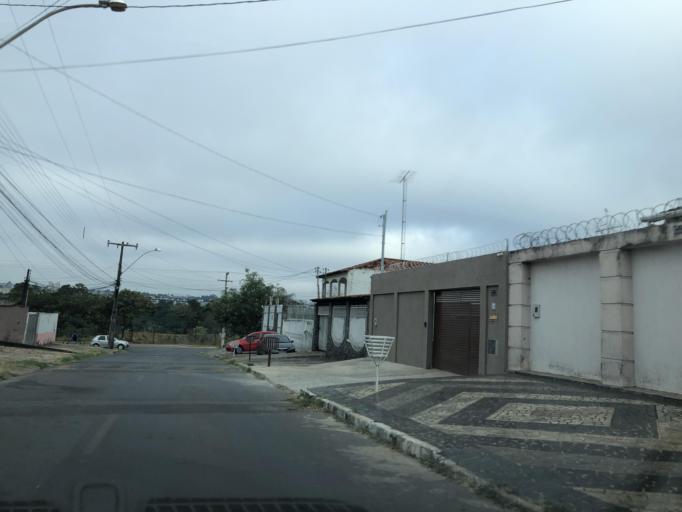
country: BR
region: Federal District
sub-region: Brasilia
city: Brasilia
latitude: -15.8149
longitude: -48.0706
